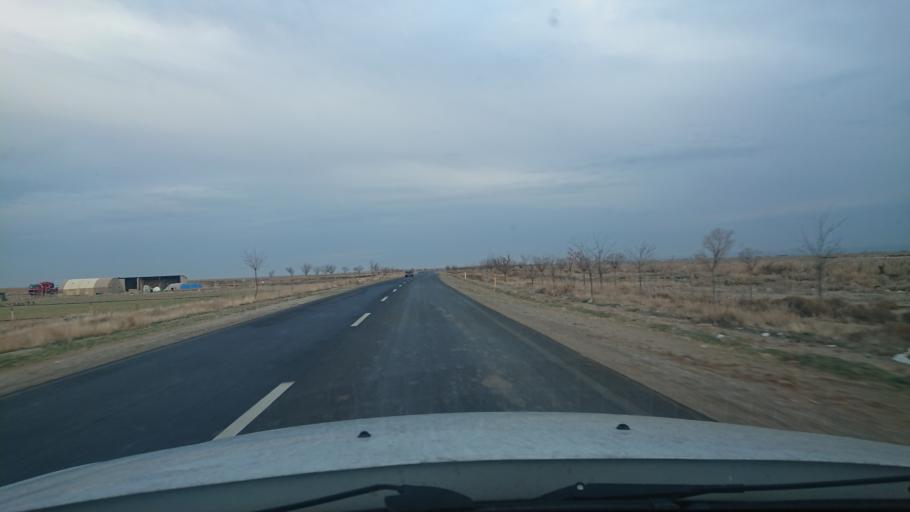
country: TR
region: Aksaray
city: Yesilova
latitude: 38.3074
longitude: 33.7548
